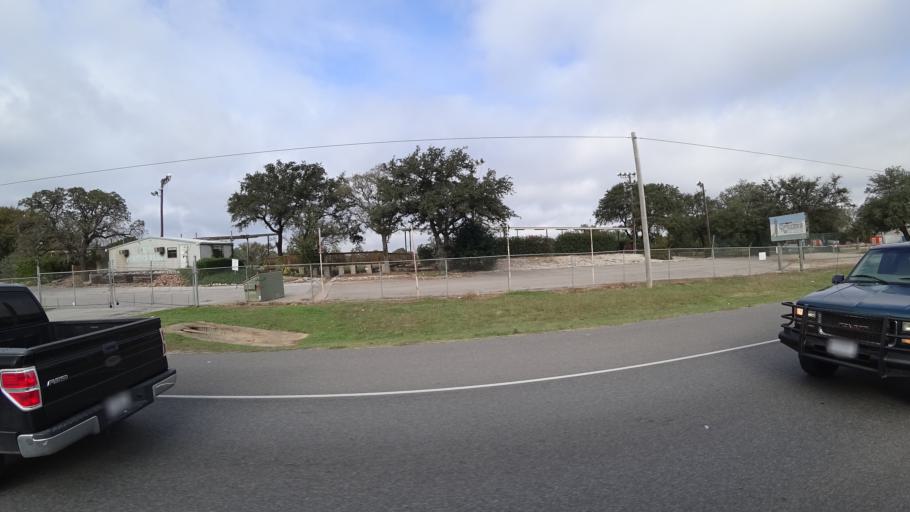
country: US
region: Texas
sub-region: Williamson County
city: Anderson Mill
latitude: 30.4519
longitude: -97.8291
